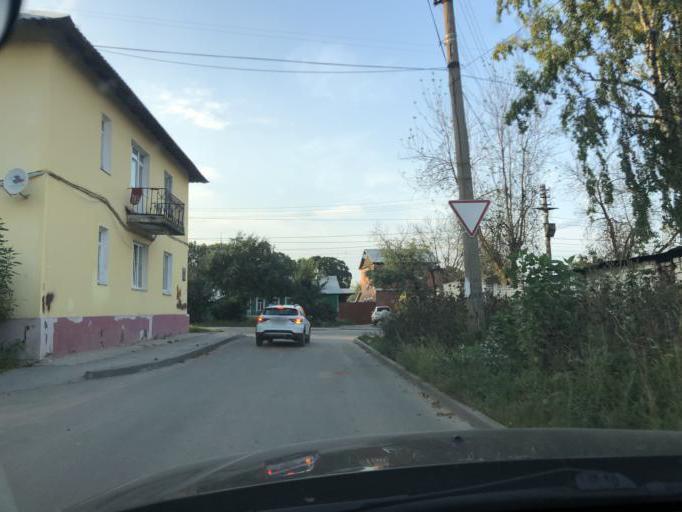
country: RU
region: Tula
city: Tula
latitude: 54.1763
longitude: 37.6283
